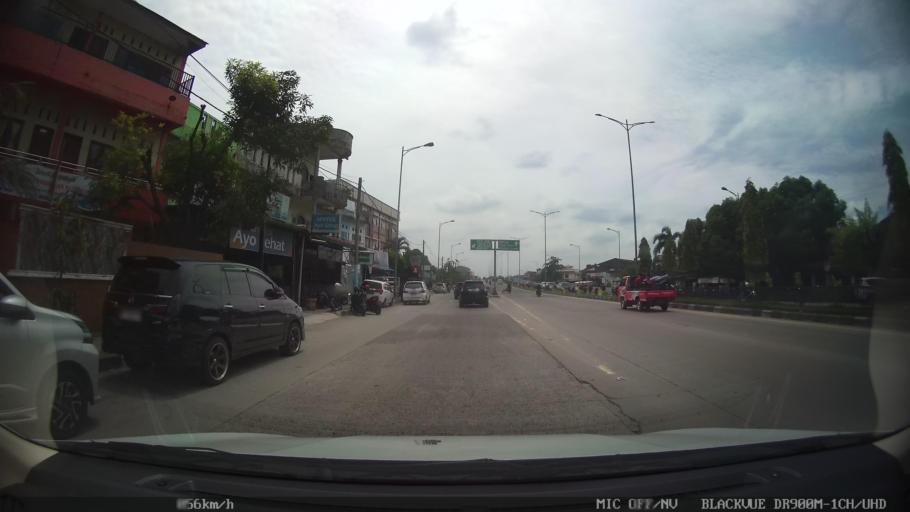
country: ID
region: North Sumatra
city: Medan
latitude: 3.5406
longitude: 98.6510
